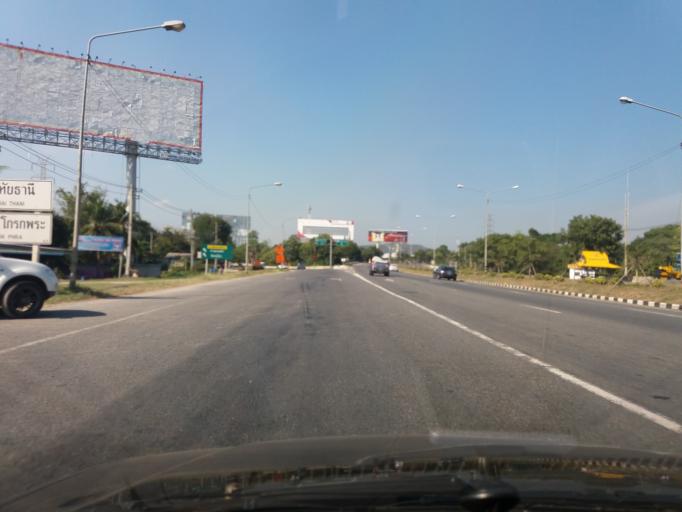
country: TH
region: Nakhon Sawan
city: Krok Phra
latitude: 15.6141
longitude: 100.1210
